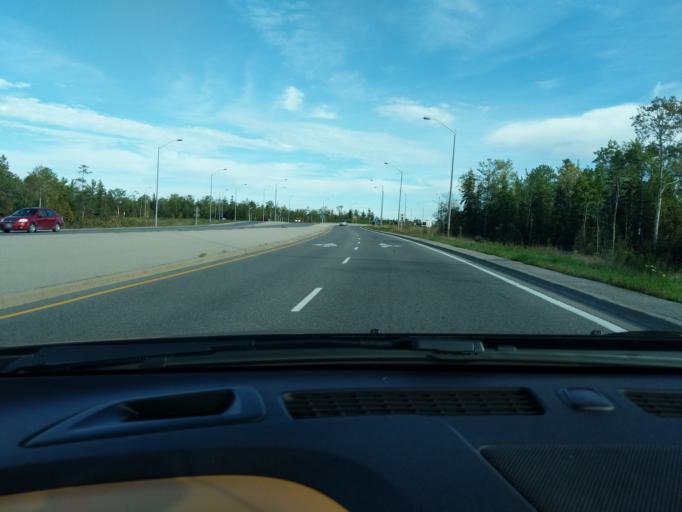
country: CA
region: Ontario
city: Collingwood
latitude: 44.4623
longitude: -80.1157
